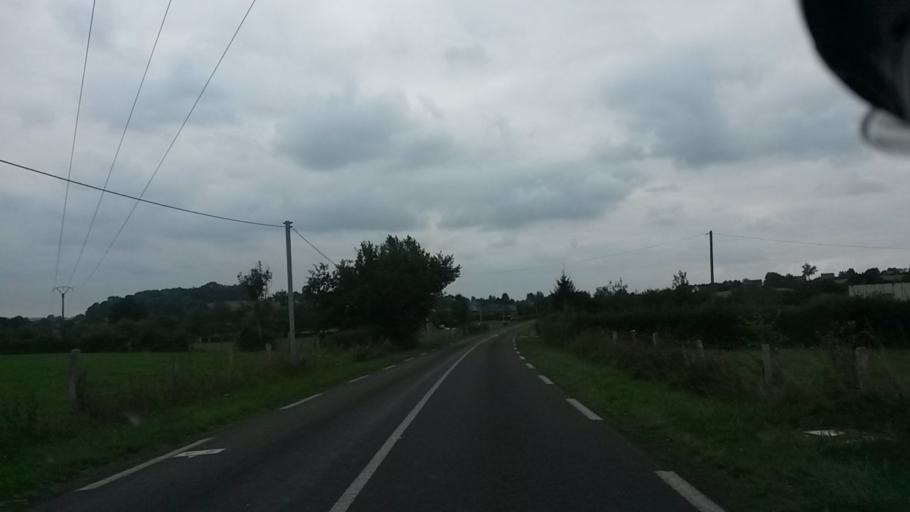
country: FR
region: Haute-Normandie
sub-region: Departement de la Seine-Maritime
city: Forges-les-Eaux
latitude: 49.5778
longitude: 1.5430
